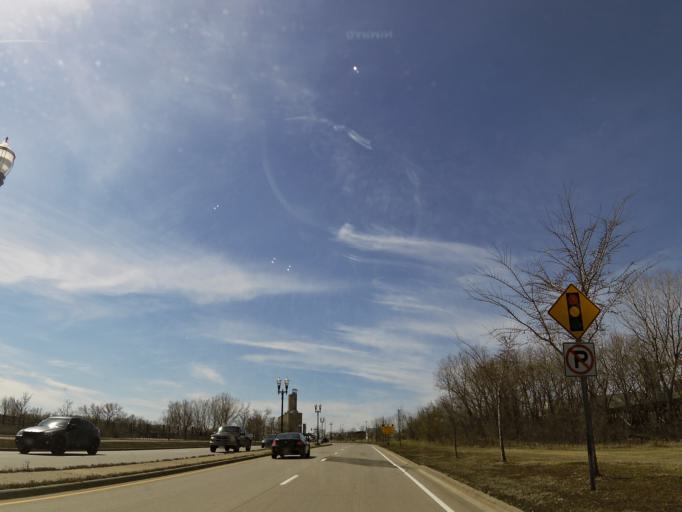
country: US
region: Minnesota
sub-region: Dakota County
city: West Saint Paul
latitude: 44.9291
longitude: -93.1180
